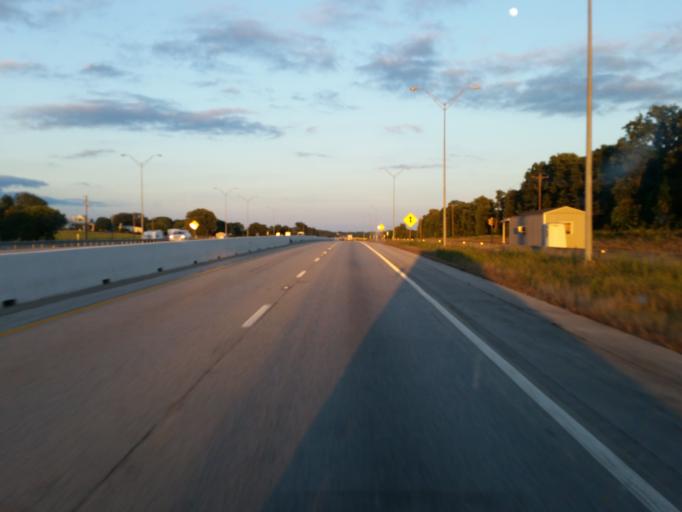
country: US
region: Texas
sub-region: Van Zandt County
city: Van
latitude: 32.4931
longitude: -95.5604
